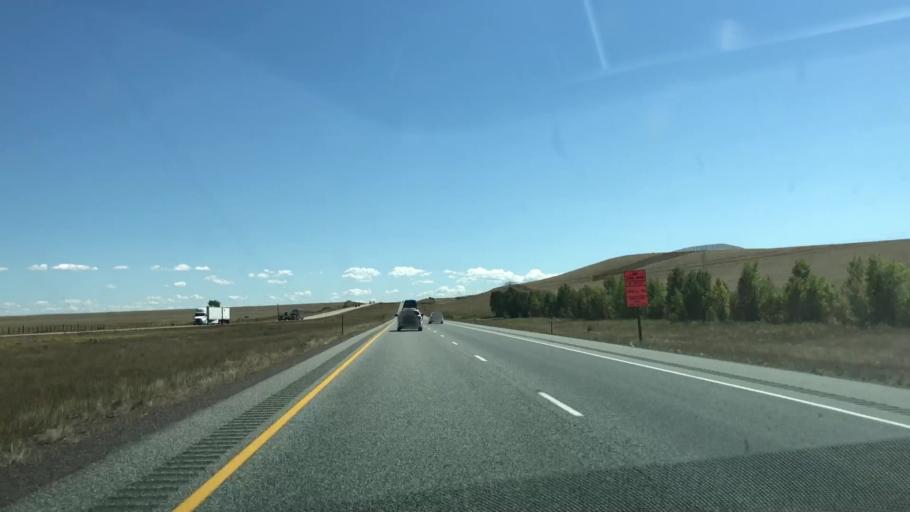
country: US
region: Wyoming
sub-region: Albany County
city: Laramie
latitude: 41.4792
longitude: -106.0152
